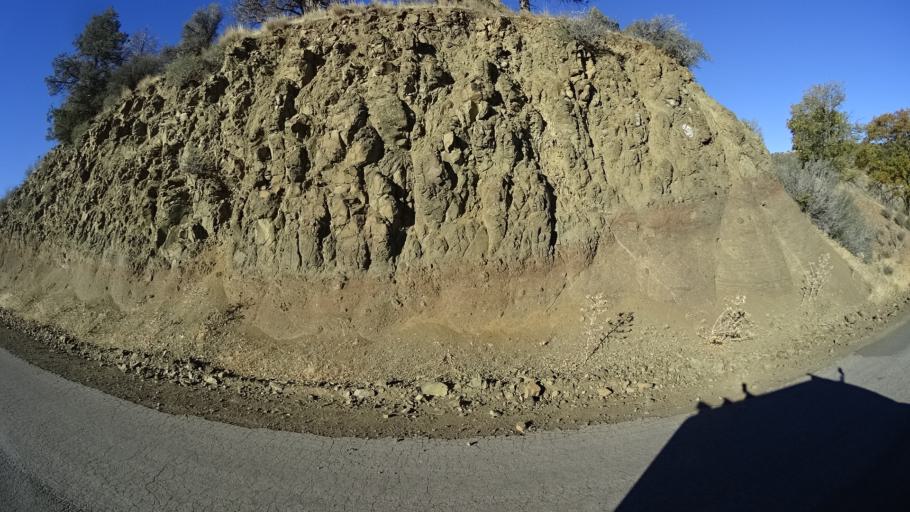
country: US
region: California
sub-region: Siskiyou County
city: Montague
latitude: 41.9445
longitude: -122.4402
